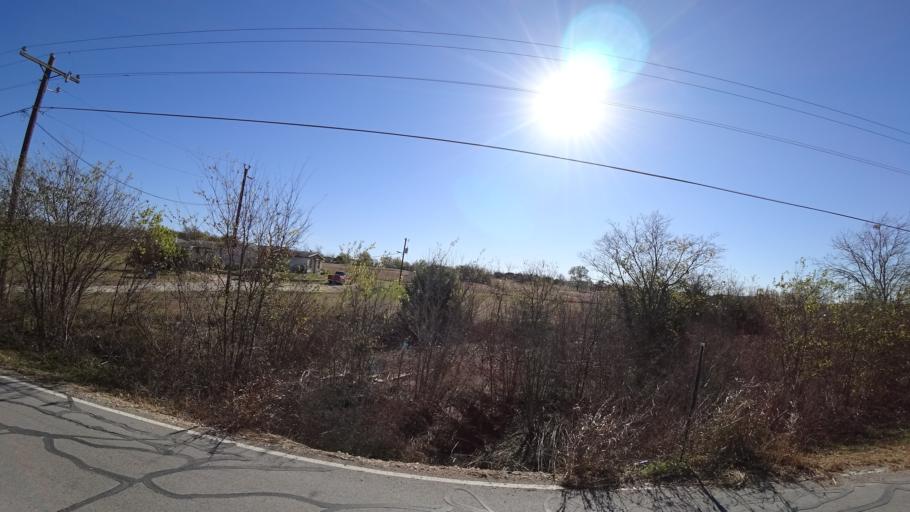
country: US
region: Texas
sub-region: Travis County
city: Onion Creek
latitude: 30.1061
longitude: -97.6753
